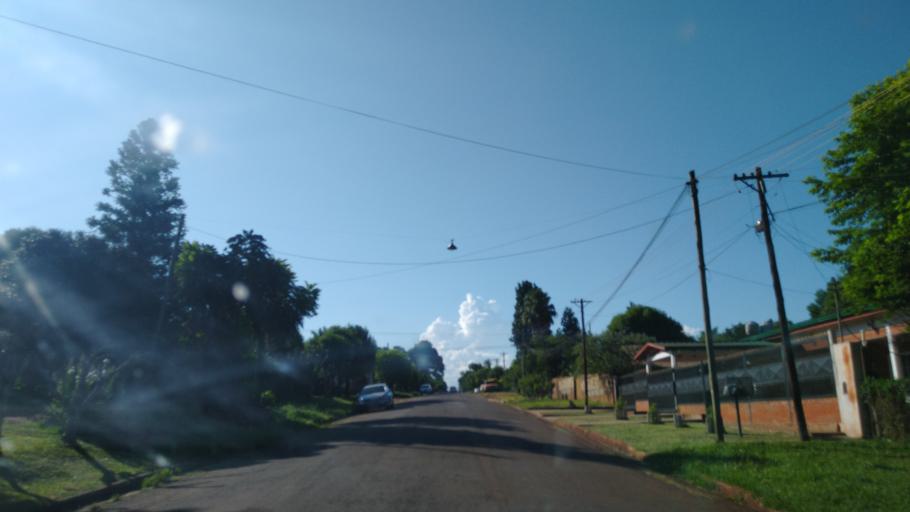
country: AR
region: Misiones
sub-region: Departamento de San Ignacio
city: San Ignacio
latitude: -27.2629
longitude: -55.5402
